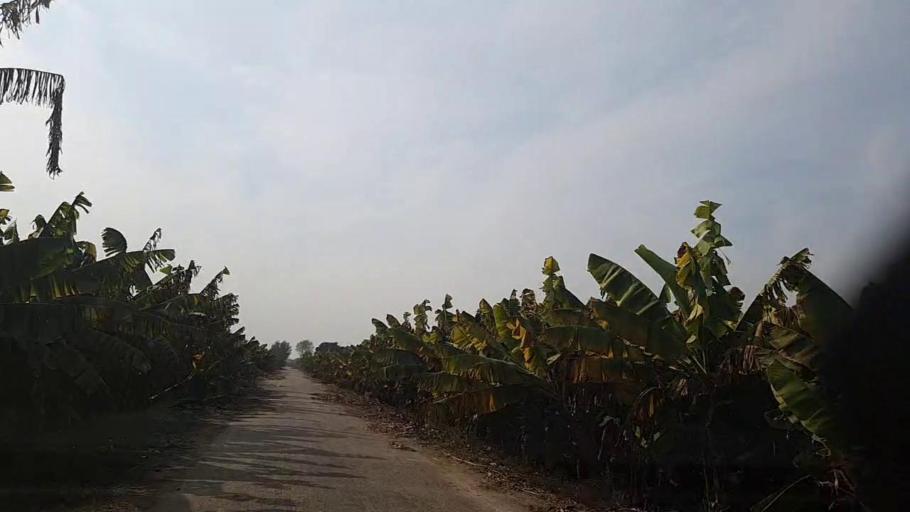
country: PK
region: Sindh
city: Daur
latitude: 26.3995
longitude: 68.2073
